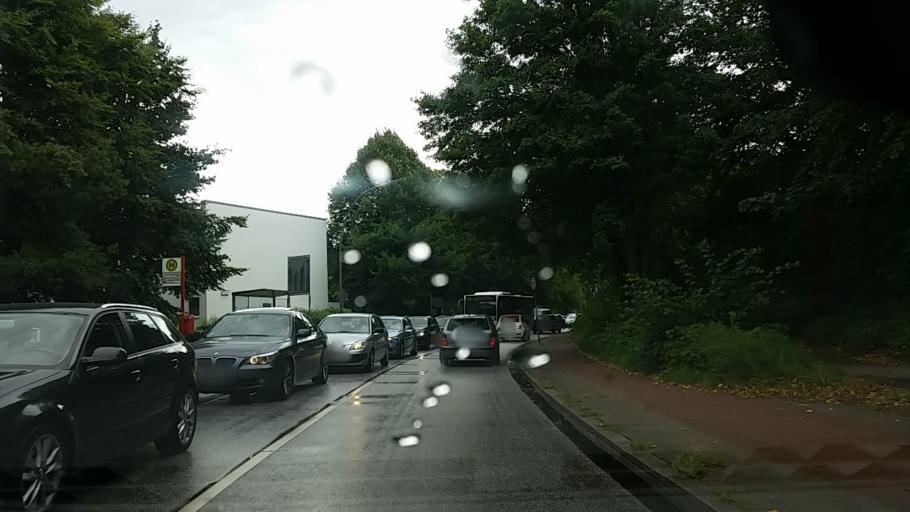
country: DE
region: Hamburg
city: Eidelstedt
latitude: 53.5694
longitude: 9.8660
